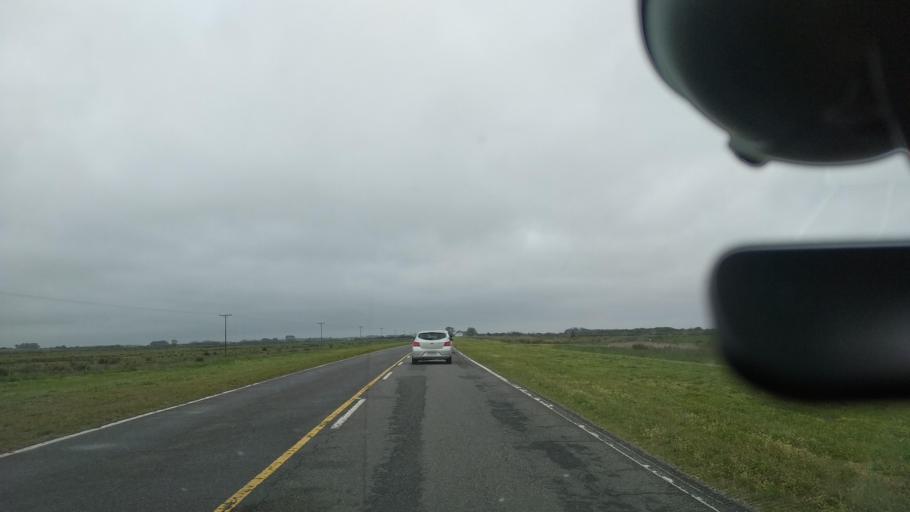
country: AR
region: Buenos Aires
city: Veronica
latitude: -35.6034
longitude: -57.2786
